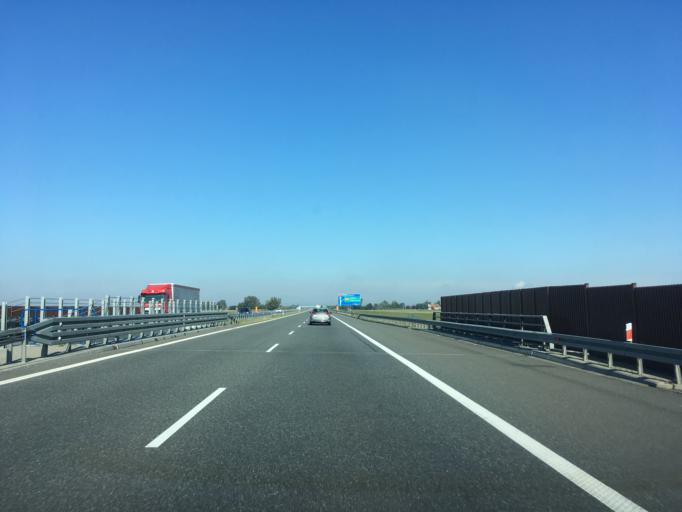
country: PL
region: Kujawsko-Pomorskie
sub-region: Powiat chelminski
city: Lisewo
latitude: 53.2684
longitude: 18.7198
